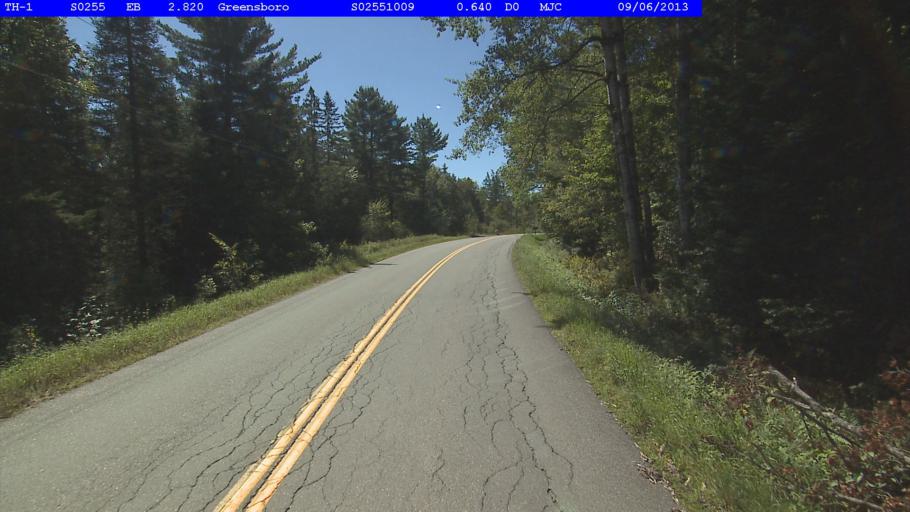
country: US
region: Vermont
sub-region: Caledonia County
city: Hardwick
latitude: 44.6316
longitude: -72.3271
